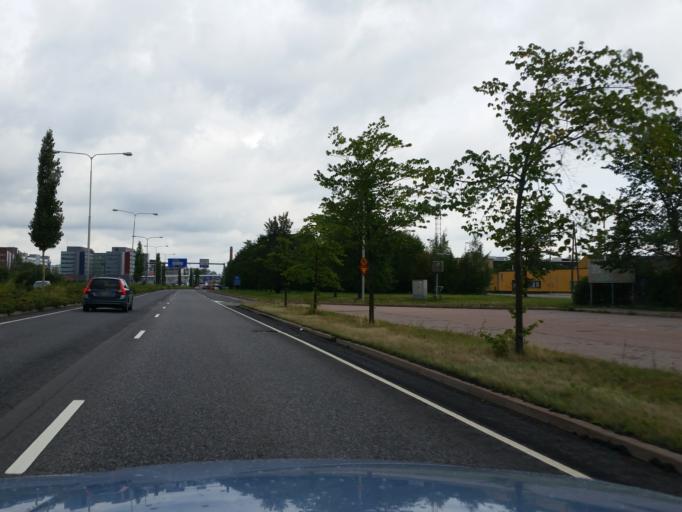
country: FI
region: Varsinais-Suomi
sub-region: Turku
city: Turku
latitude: 60.4462
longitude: 22.3051
